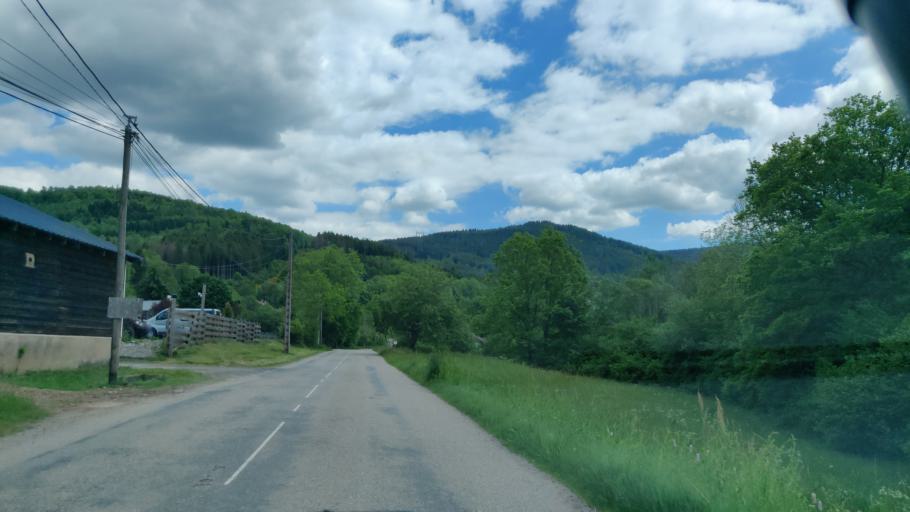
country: FR
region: Lorraine
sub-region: Departement des Vosges
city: Fraize
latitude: 48.1645
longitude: 6.9827
